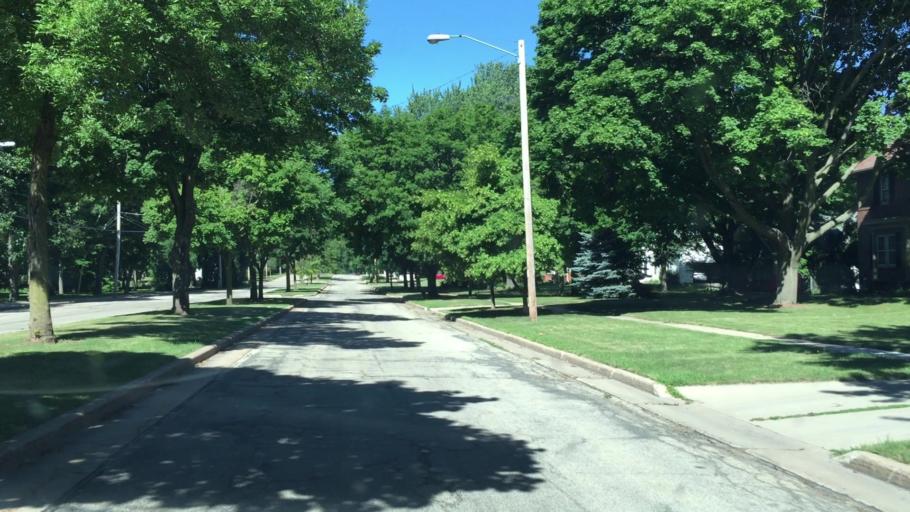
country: US
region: Wisconsin
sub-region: Winnebago County
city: Menasha
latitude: 44.1936
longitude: -88.4362
